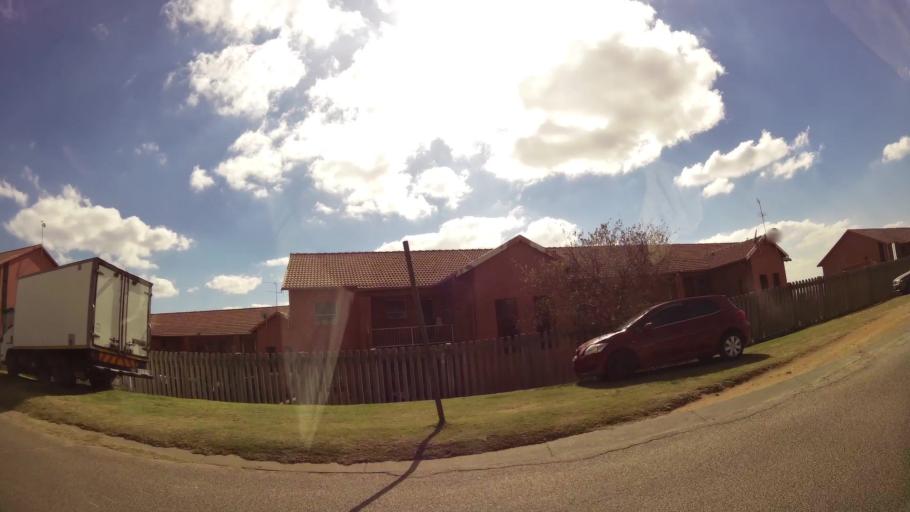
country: ZA
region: Gauteng
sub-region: Ekurhuleni Metropolitan Municipality
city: Tembisa
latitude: -26.0287
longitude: 28.1759
